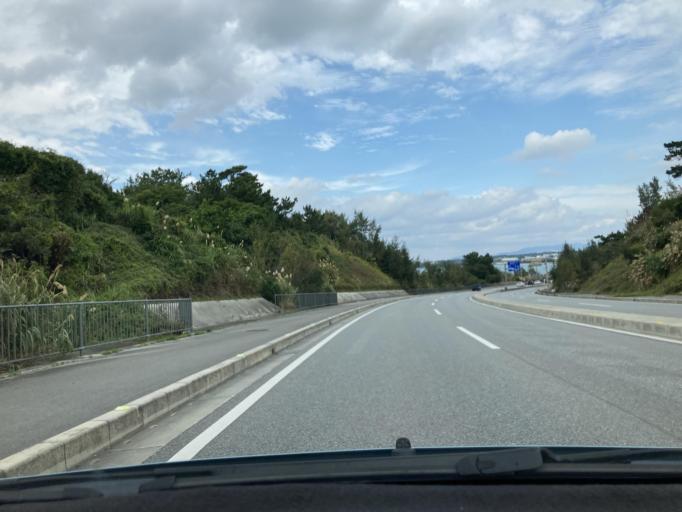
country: JP
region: Okinawa
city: Ishikawa
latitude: 26.4753
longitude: 127.8389
